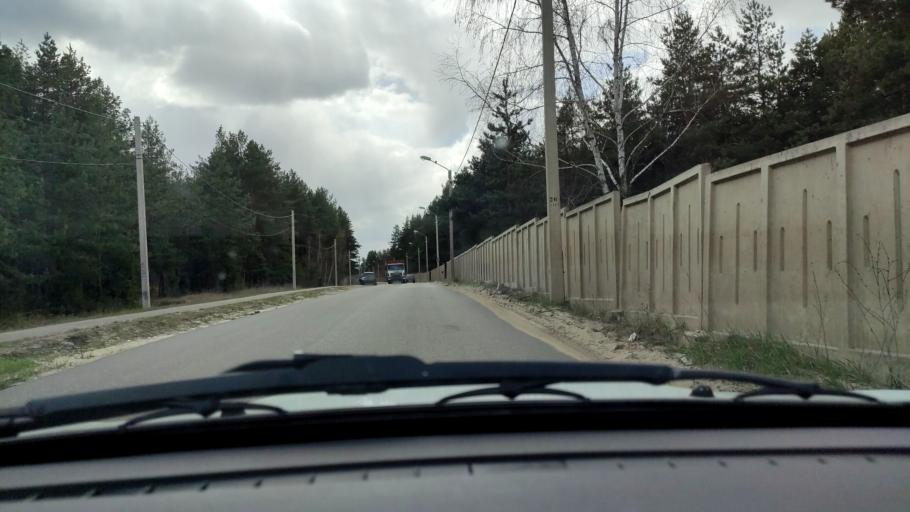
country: RU
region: Voronezj
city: Pridonskoy
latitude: 51.6961
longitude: 39.1048
